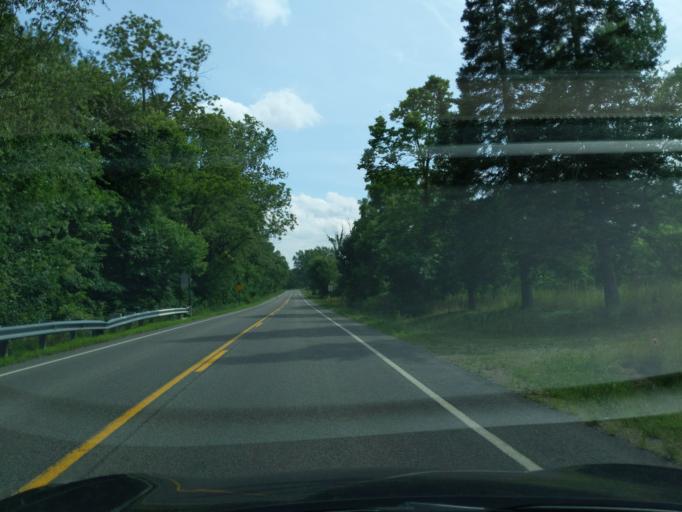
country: US
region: Michigan
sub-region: Eaton County
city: Dimondale
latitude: 42.5883
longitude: -84.6026
